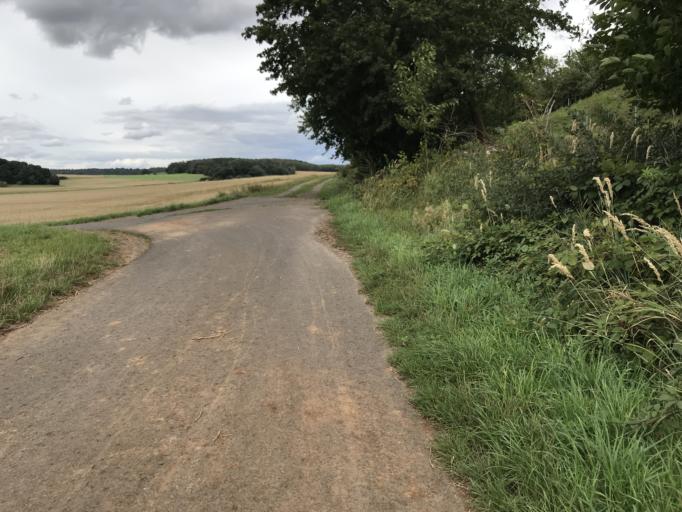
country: DE
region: Hesse
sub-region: Regierungsbezirk Giessen
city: Grunberg
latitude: 50.5561
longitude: 8.9173
